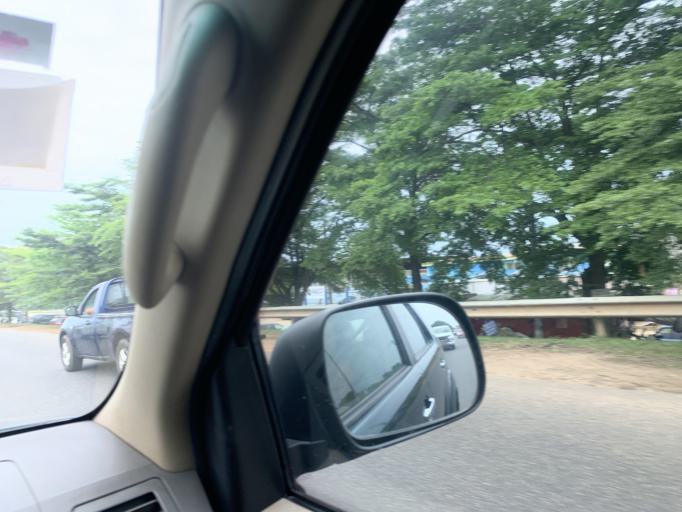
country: GA
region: Estuaire
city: Libreville
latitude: 0.3413
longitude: 9.4765
